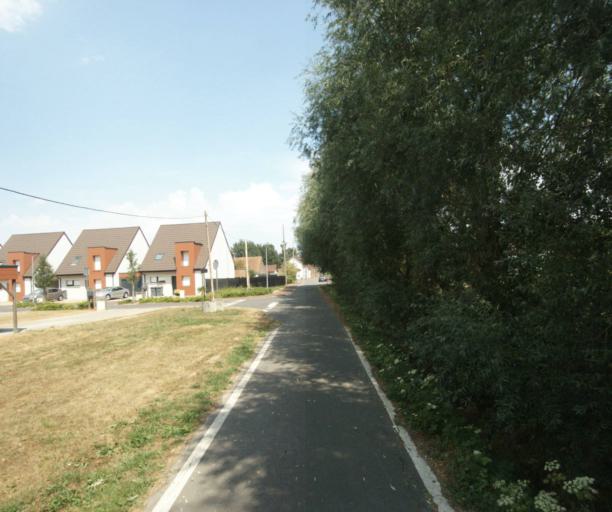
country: FR
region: Nord-Pas-de-Calais
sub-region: Departement du Nord
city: Comines
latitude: 50.7560
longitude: 2.9877
